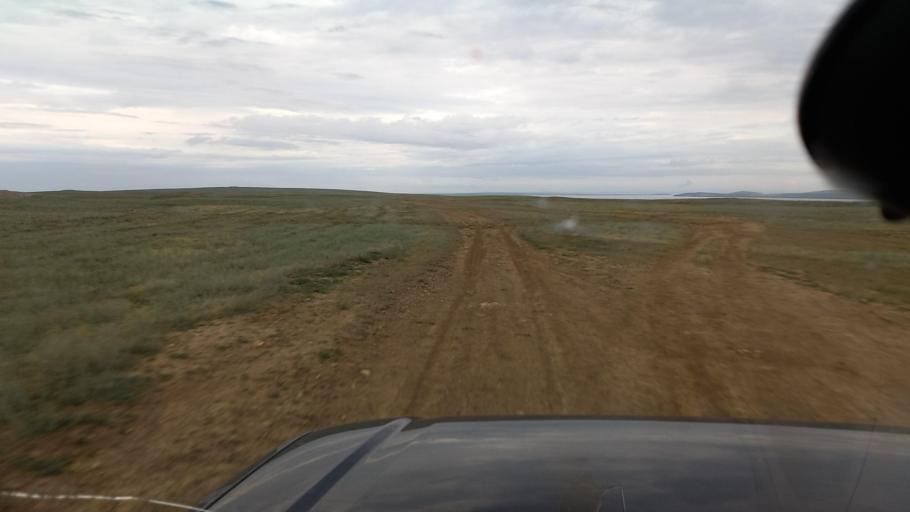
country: RU
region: Krasnodarskiy
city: Taman'
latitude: 45.2015
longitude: 36.7851
